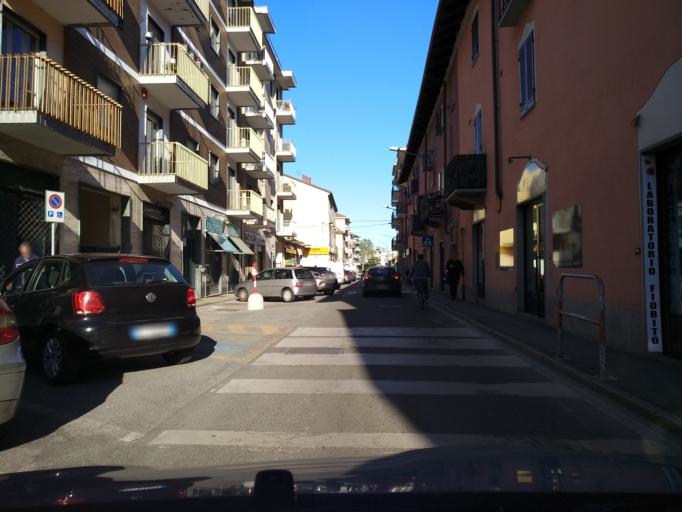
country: IT
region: Piedmont
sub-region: Provincia di Torino
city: Pinerolo
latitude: 44.8842
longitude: 7.3363
